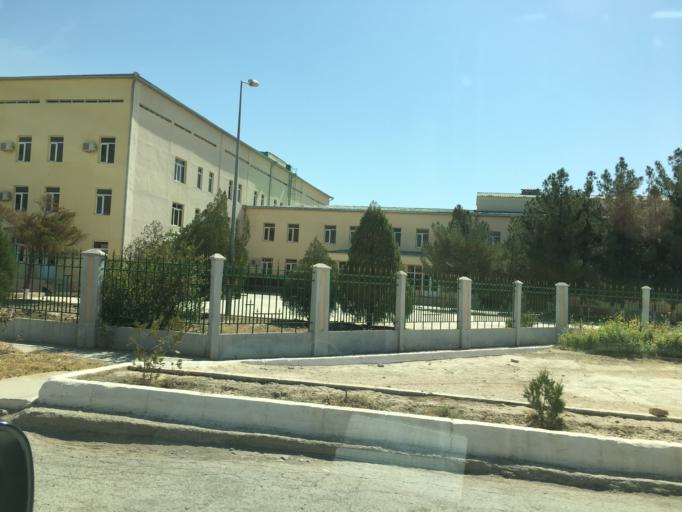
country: IR
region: Razavi Khorasan
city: Sarakhs
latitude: 36.5335
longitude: 61.2204
